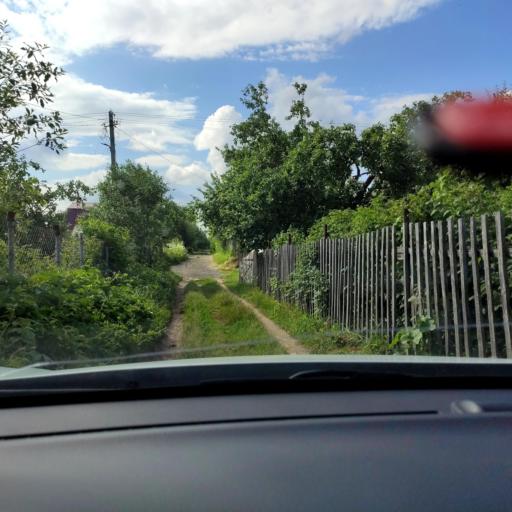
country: RU
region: Tatarstan
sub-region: Gorod Kazan'
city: Kazan
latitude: 55.8892
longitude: 49.0631
